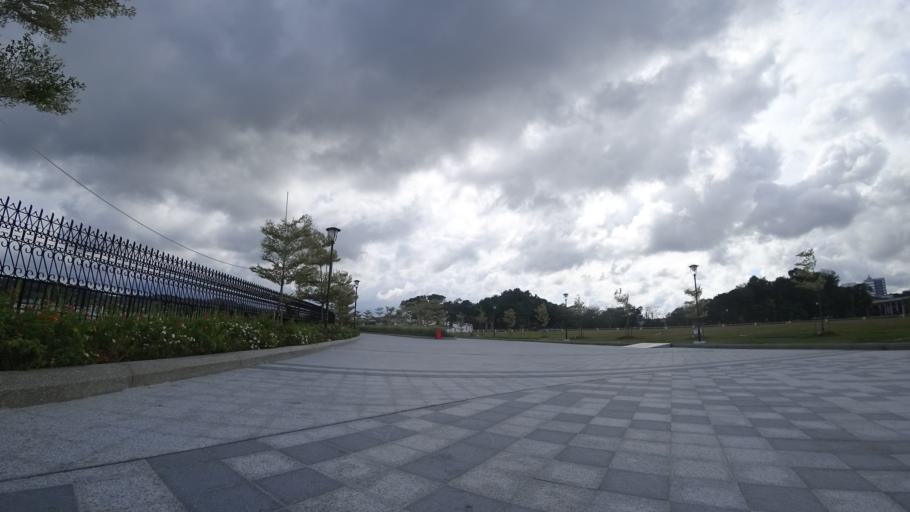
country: BN
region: Brunei and Muara
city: Bandar Seri Begawan
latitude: 4.8899
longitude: 114.9381
